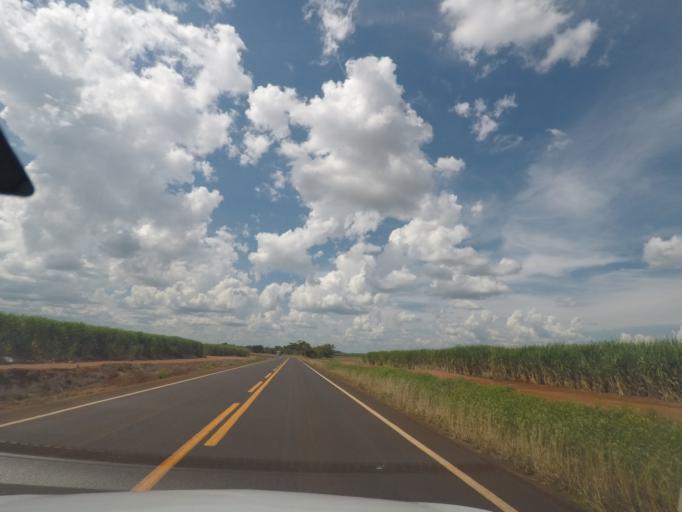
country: BR
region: Minas Gerais
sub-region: Conceicao Das Alagoas
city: Conceicao das Alagoas
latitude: -19.8372
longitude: -48.5905
